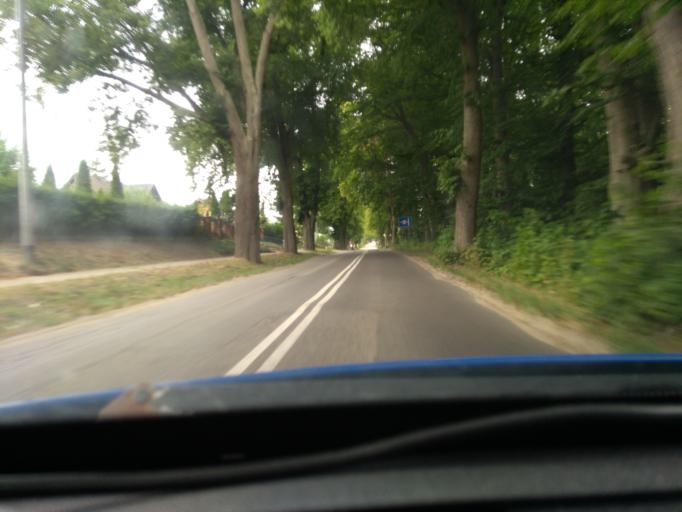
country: PL
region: Pomeranian Voivodeship
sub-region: Powiat kartuski
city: Banino
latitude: 54.3701
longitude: 18.3897
